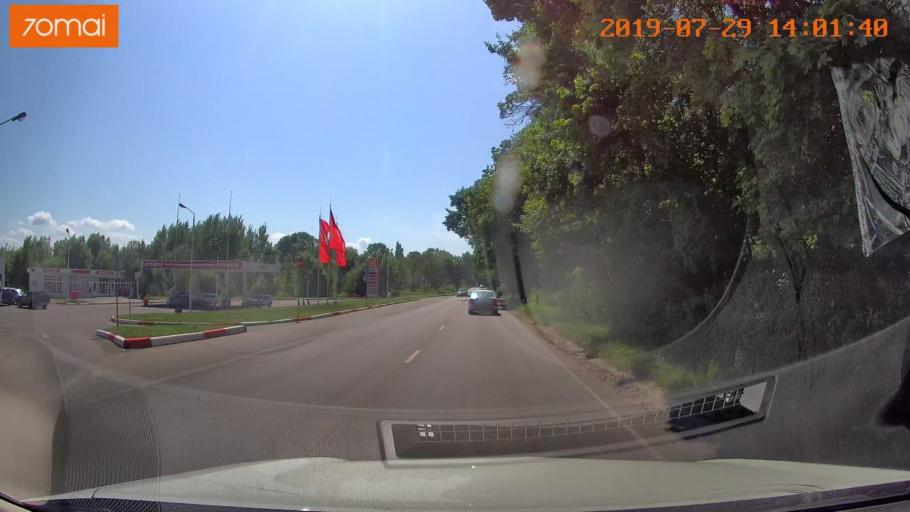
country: RU
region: Kaliningrad
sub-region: Gorod Kaliningrad
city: Baltiysk
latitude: 54.6686
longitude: 19.9200
